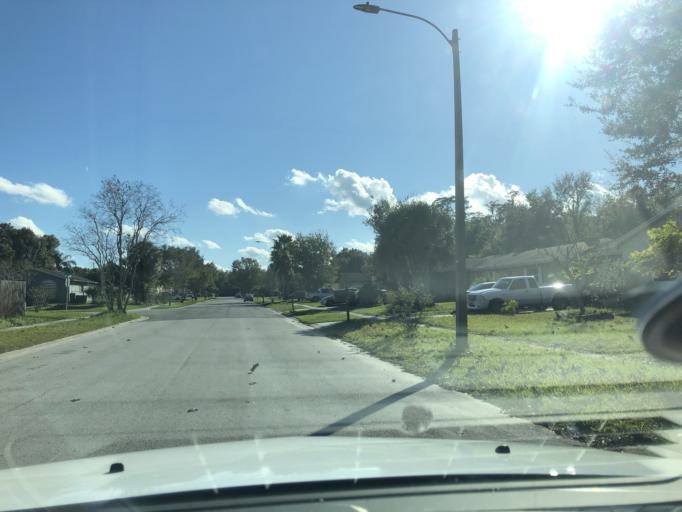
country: US
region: Florida
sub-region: Orange County
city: Oak Ridge
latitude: 28.4770
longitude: -81.4377
